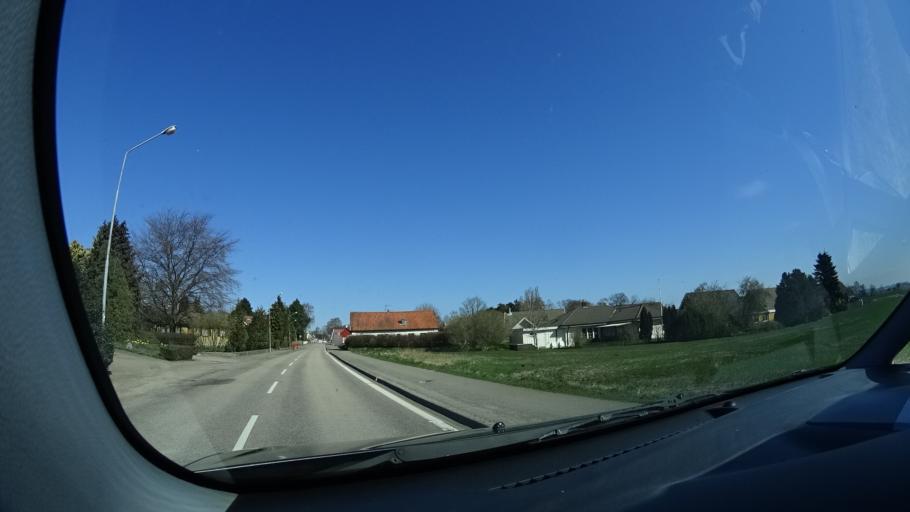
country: SE
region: Skane
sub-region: Hoganas Kommun
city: Hoganas
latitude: 56.2232
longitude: 12.6744
